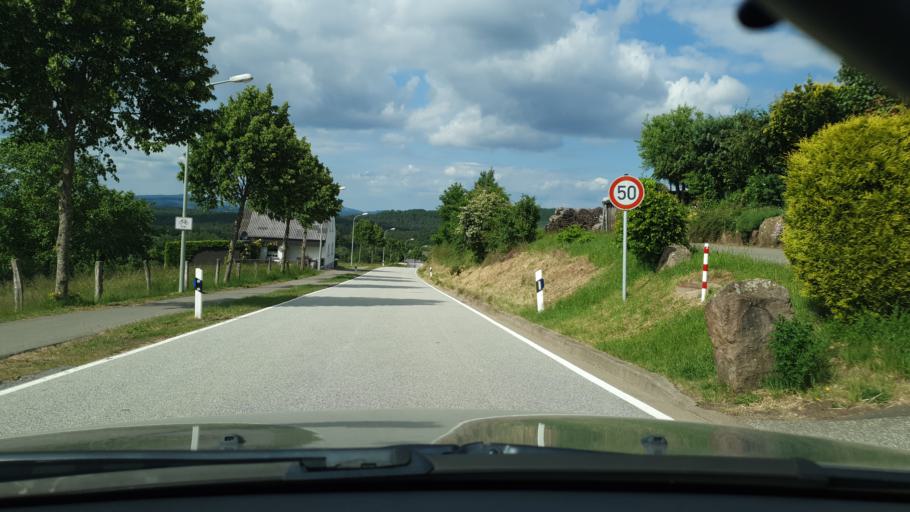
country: DE
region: Rheinland-Pfalz
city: Martinshohe
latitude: 49.3666
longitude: 7.4800
